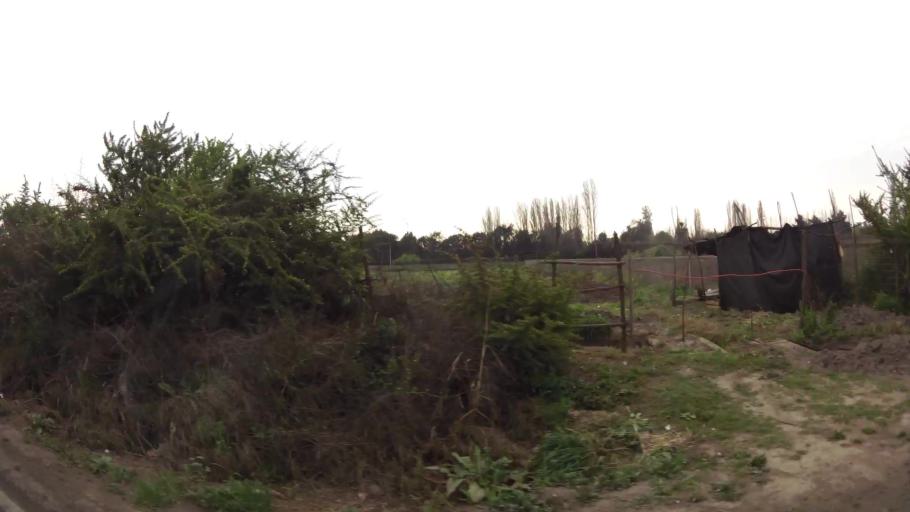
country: CL
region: Santiago Metropolitan
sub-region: Provincia de Chacabuco
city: Chicureo Abajo
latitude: -33.2624
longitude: -70.7130
